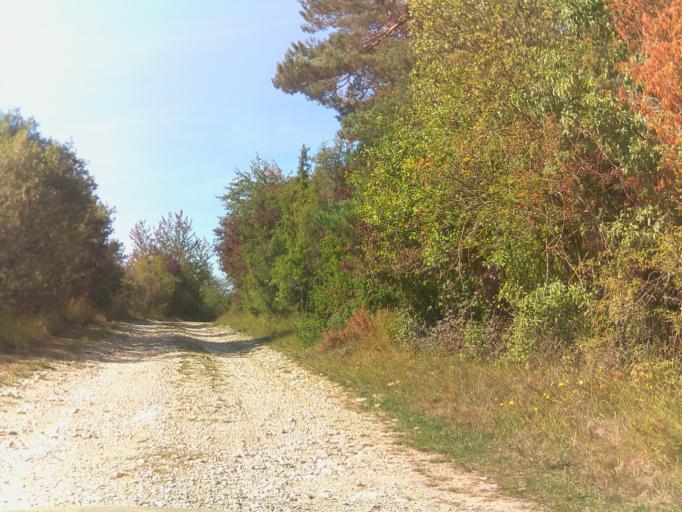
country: DE
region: Thuringia
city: Rottenbach
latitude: 50.7493
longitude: 11.1953
